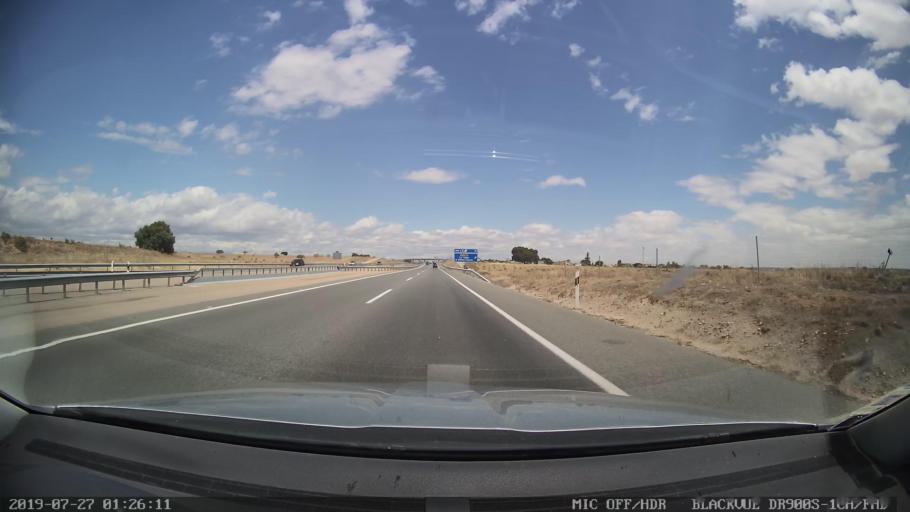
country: ES
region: Castille-La Mancha
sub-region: Province of Toledo
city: La Torre de Esteban Hambran
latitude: 40.1526
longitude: -4.1761
